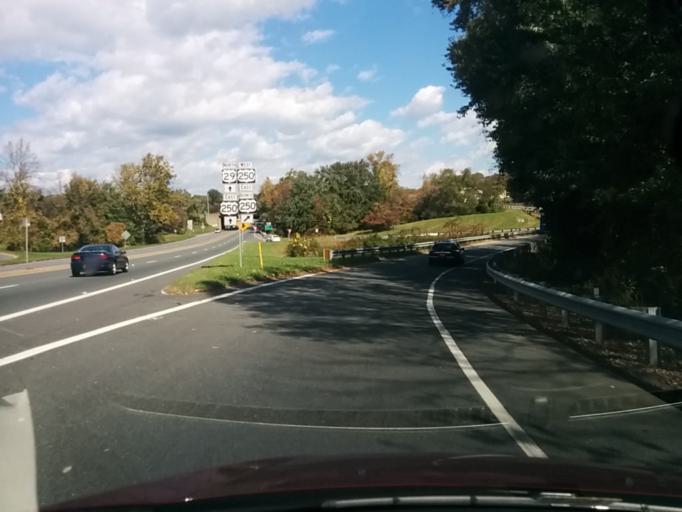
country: US
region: Virginia
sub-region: City of Charlottesville
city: Charlottesville
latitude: 38.0455
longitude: -78.5257
